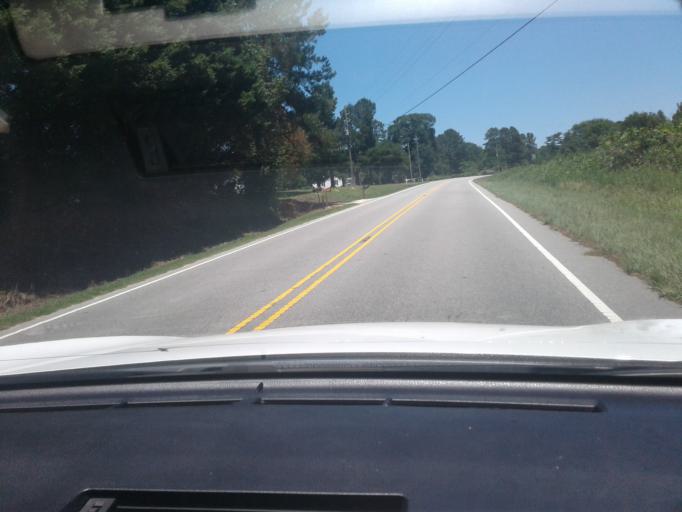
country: US
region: North Carolina
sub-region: Harnett County
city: Lillington
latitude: 35.3799
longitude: -78.8454
